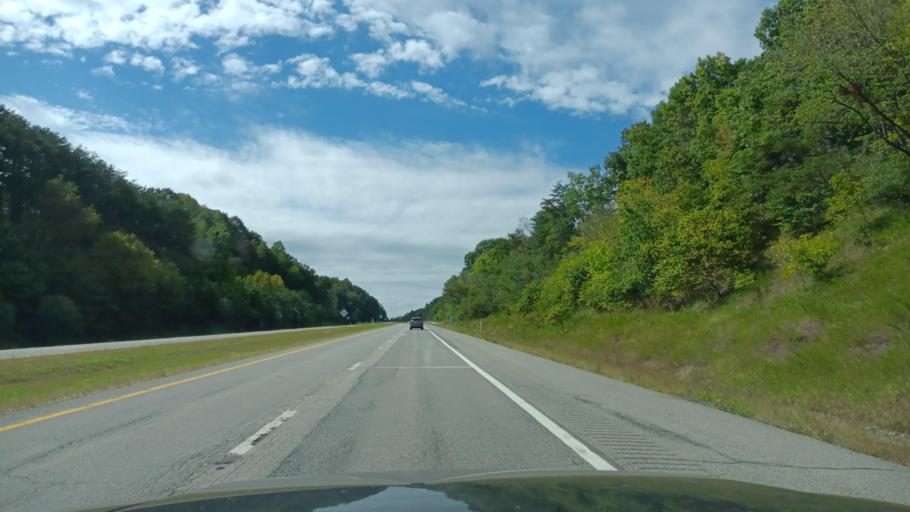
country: US
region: West Virginia
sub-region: Ritchie County
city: Harrisville
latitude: 39.2614
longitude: -81.1477
